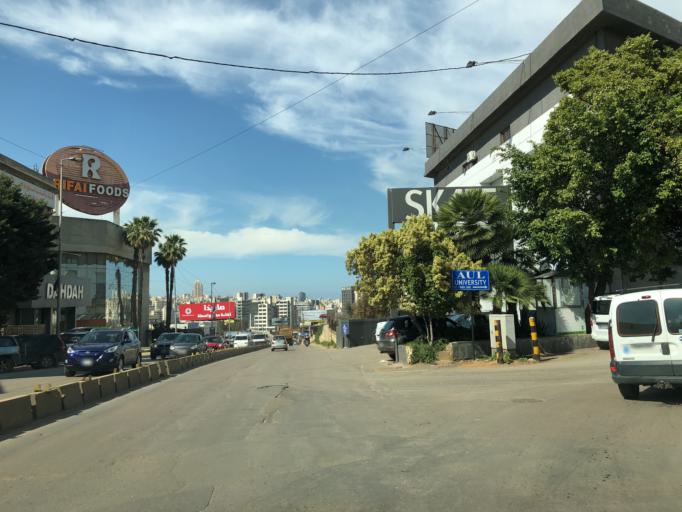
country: LB
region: Mont-Liban
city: Baabda
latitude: 33.8657
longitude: 35.5458
